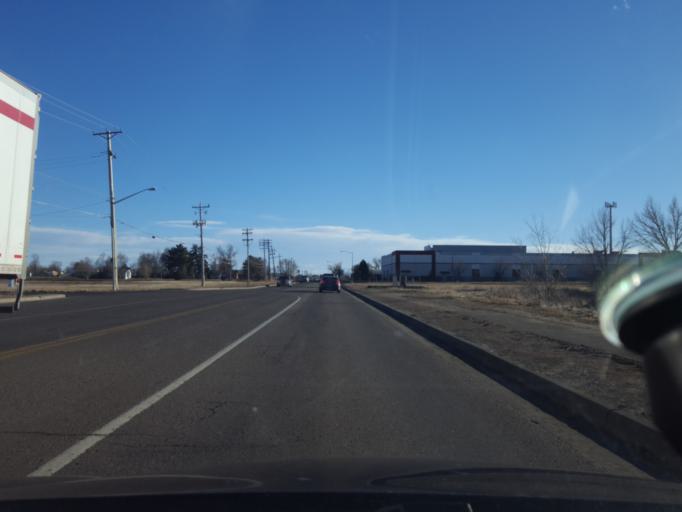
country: US
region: Colorado
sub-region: Adams County
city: Aurora
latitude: 39.7510
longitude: -104.7724
